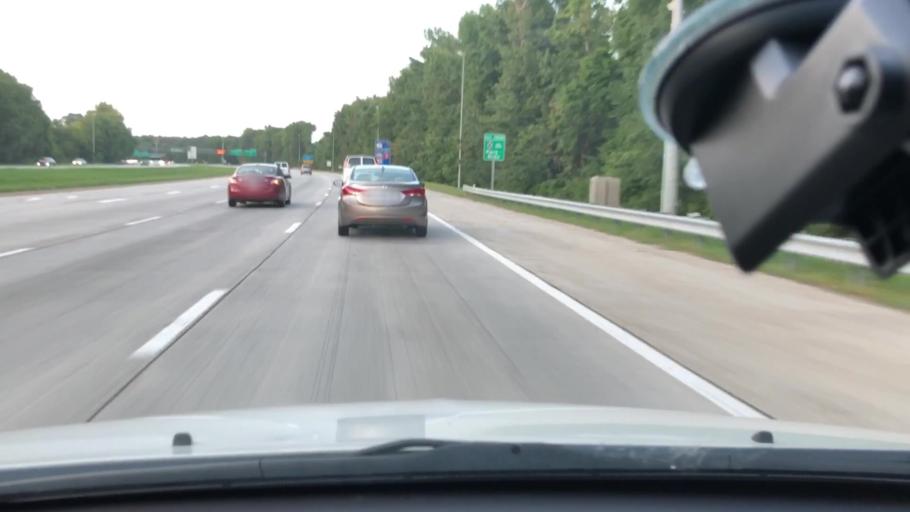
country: US
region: Virginia
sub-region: City of Chesapeake
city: Chesapeake
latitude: 36.8004
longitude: -76.2003
